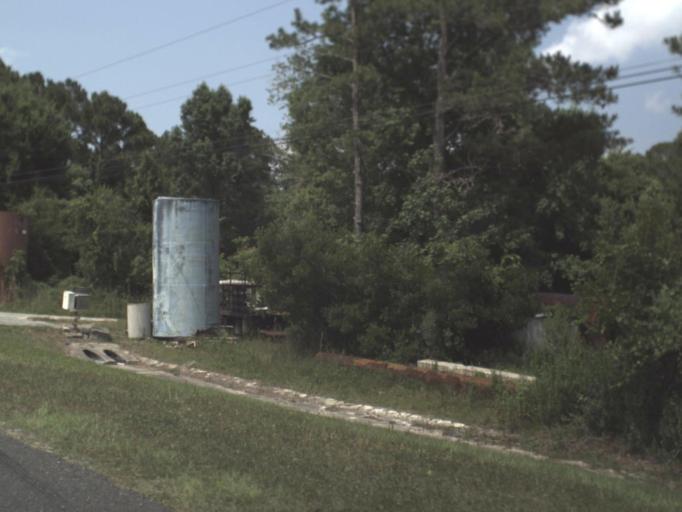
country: US
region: Florida
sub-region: Clay County
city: Green Cove Springs
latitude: 29.8802
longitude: -81.6644
